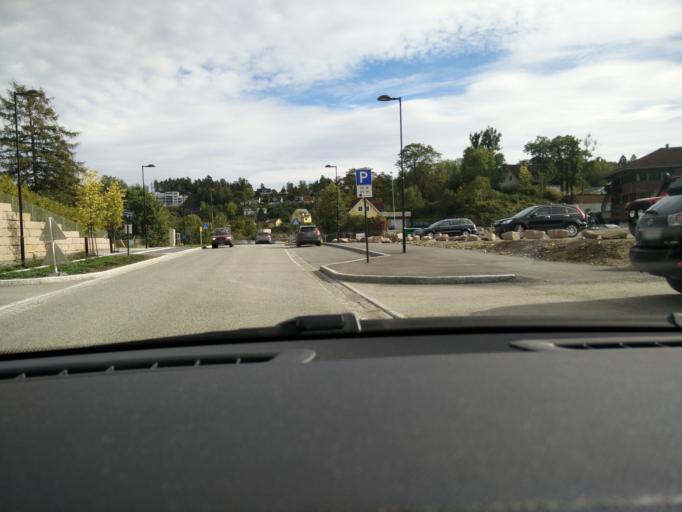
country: NO
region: Akershus
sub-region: Asker
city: Blakstad
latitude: 59.7876
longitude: 10.4355
